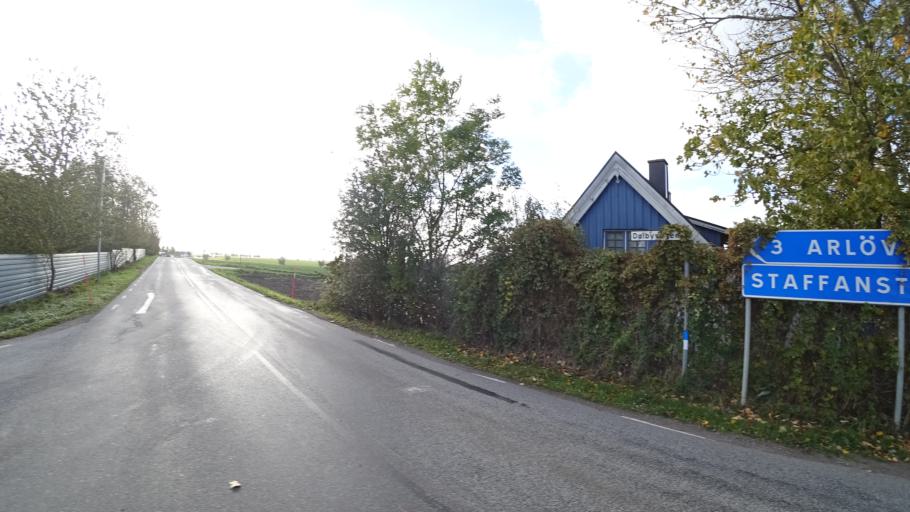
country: SE
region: Skane
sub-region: Staffanstorps Kommun
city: Hjaerup
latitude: 55.6369
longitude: 13.1176
